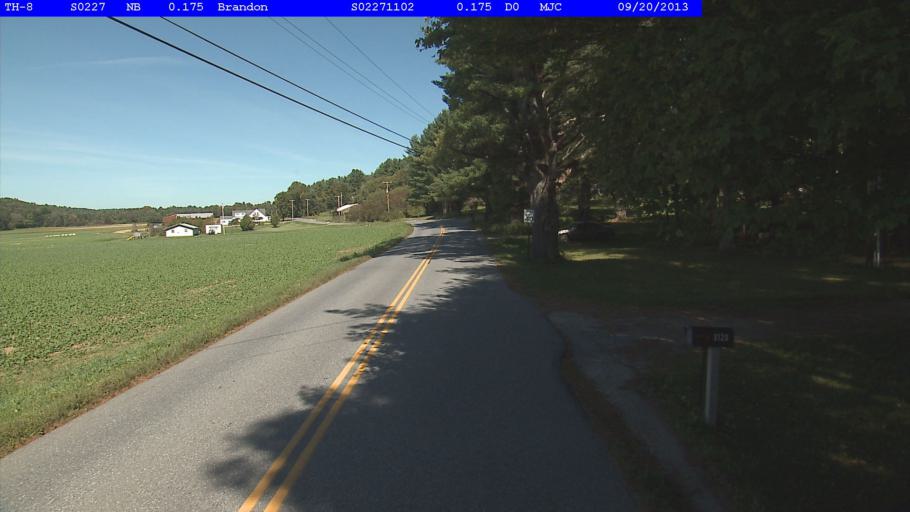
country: US
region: Vermont
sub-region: Rutland County
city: Brandon
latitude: 43.7769
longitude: -73.0524
